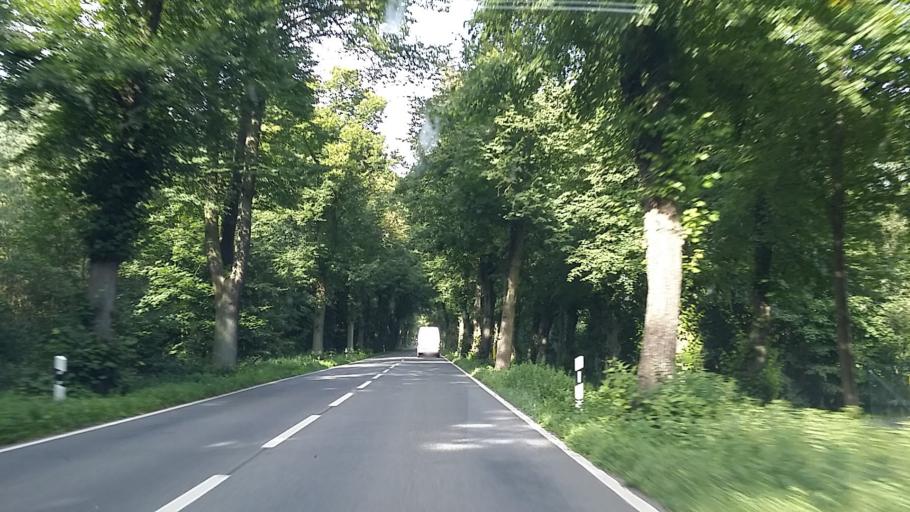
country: DE
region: Brandenburg
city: Perleberg
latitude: 53.0633
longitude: 11.8430
